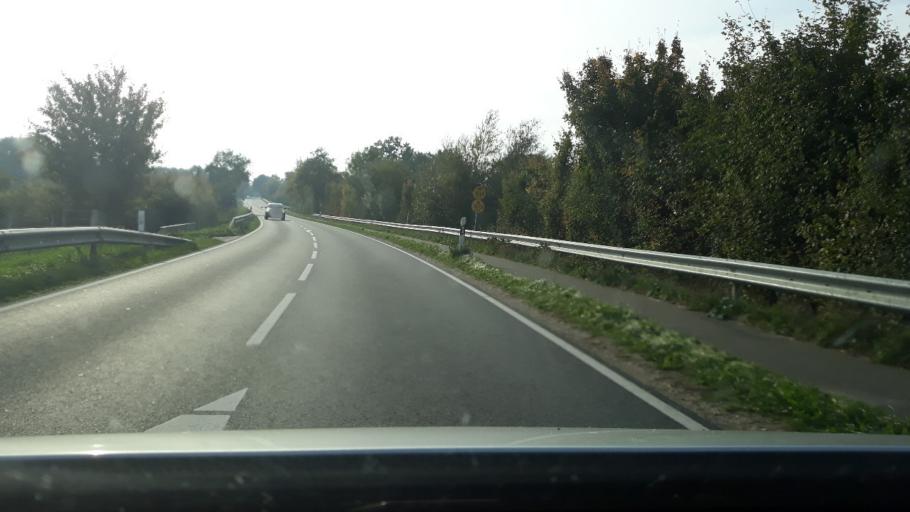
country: DE
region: Schleswig-Holstein
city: Owschlag
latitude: 54.4012
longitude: 9.5913
